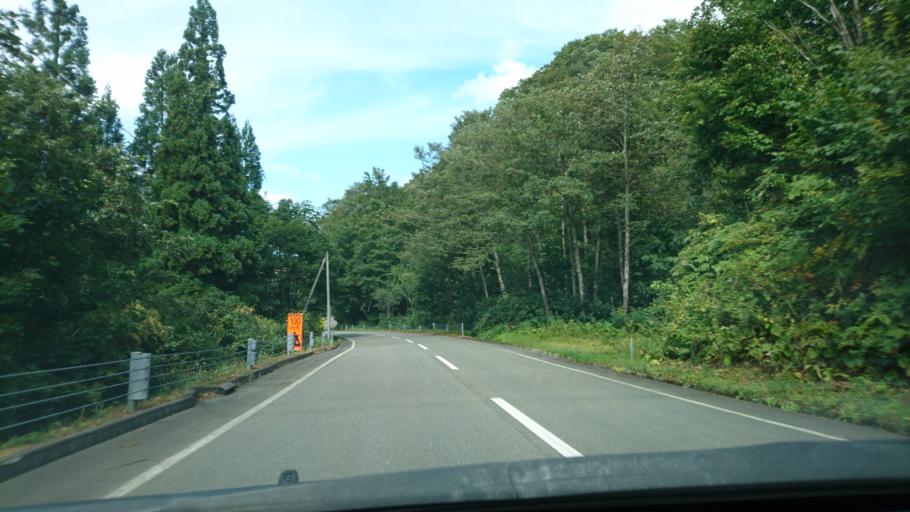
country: JP
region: Akita
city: Yuzawa
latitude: 39.0257
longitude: 140.7283
